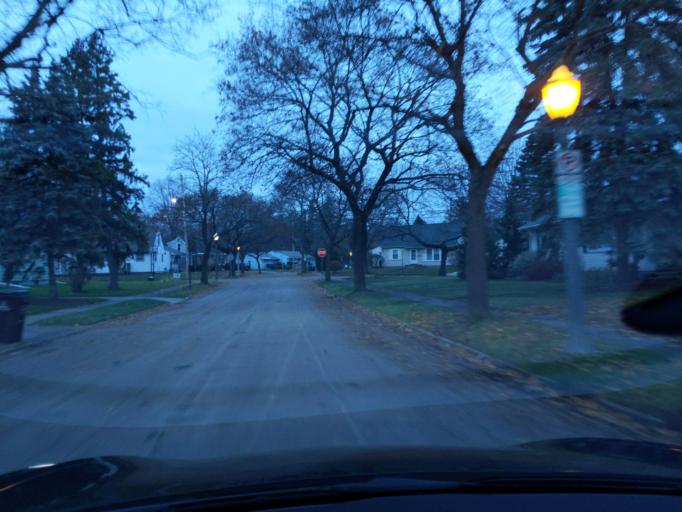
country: US
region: Michigan
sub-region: Ingham County
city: Lansing
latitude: 42.7030
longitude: -84.5578
